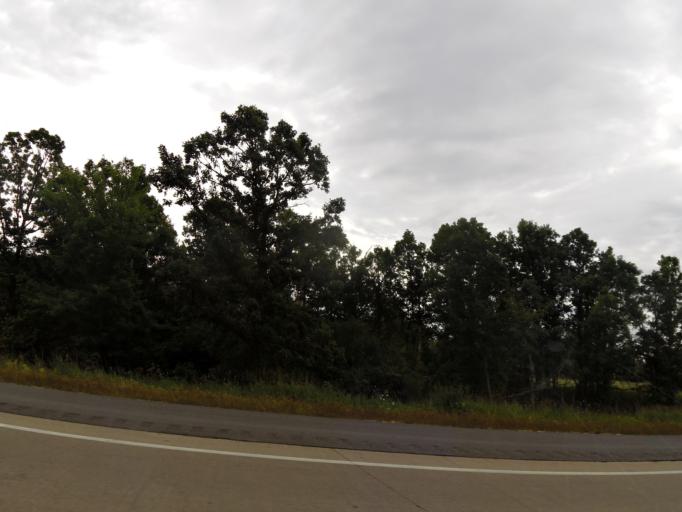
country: US
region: Wisconsin
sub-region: Monroe County
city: Tomah
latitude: 43.9495
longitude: -90.5444
